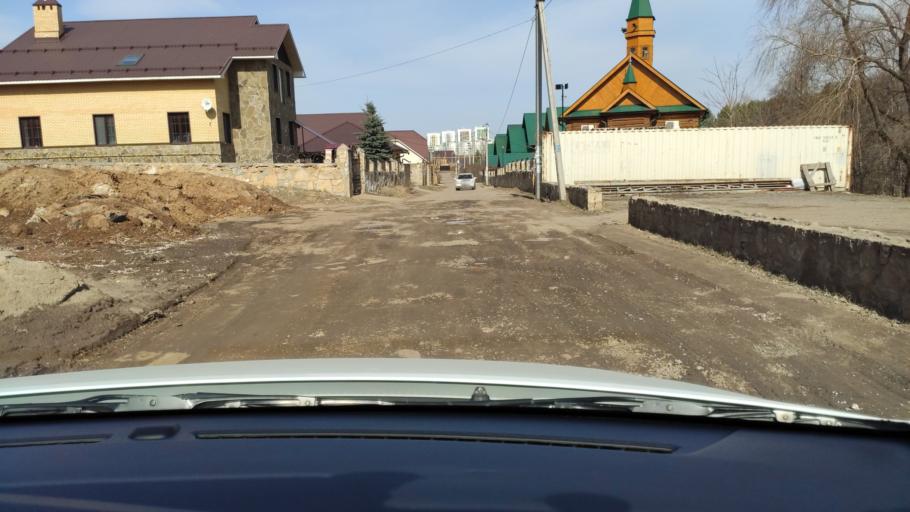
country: RU
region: Tatarstan
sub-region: Gorod Kazan'
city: Kazan
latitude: 55.7821
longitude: 49.2478
